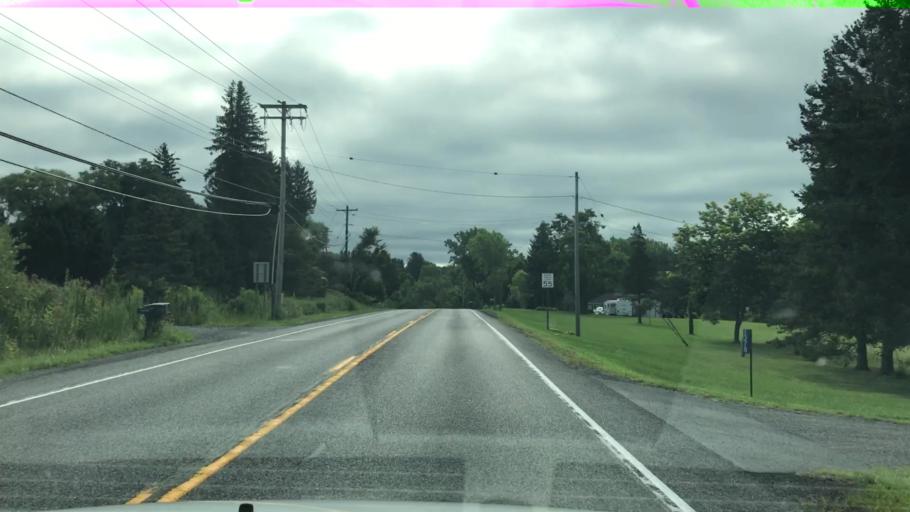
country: US
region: New York
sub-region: Wyoming County
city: Attica
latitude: 42.8362
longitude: -78.3916
